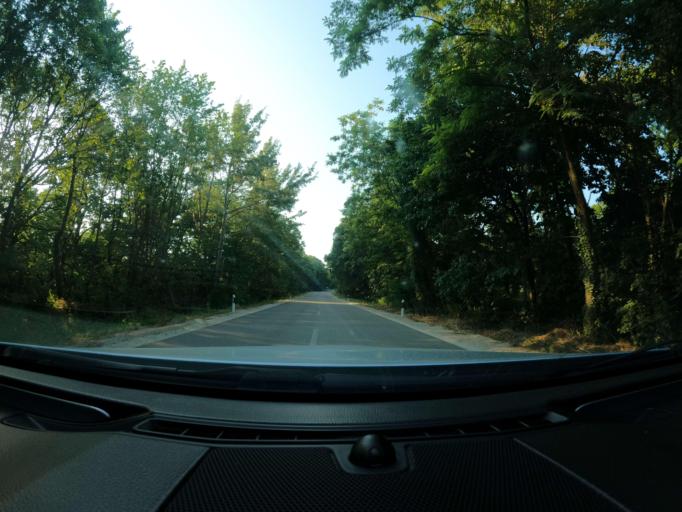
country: RS
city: Vrdnik
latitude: 45.1322
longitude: 19.7245
